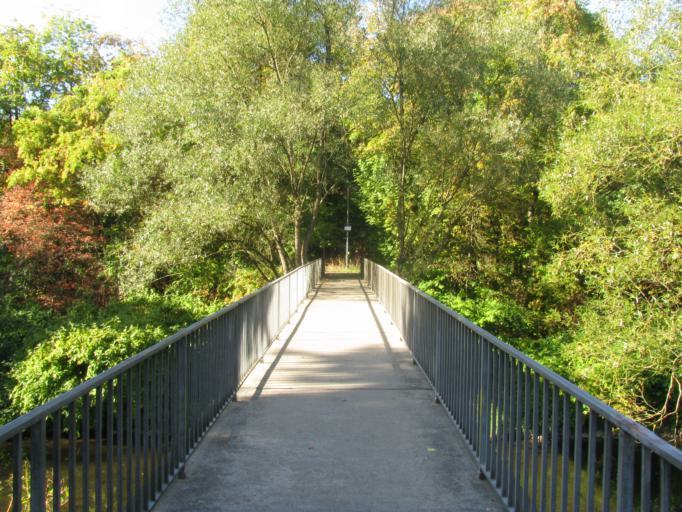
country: DE
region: North Rhine-Westphalia
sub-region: Regierungsbezirk Arnsberg
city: Siegen
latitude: 50.8565
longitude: 8.0064
